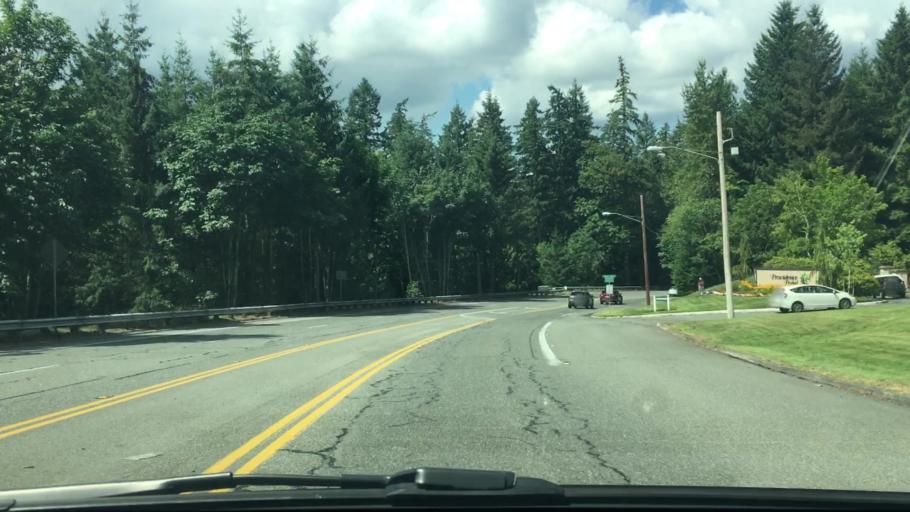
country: US
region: Washington
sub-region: King County
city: City of Sammamish
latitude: 47.5672
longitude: -122.0381
